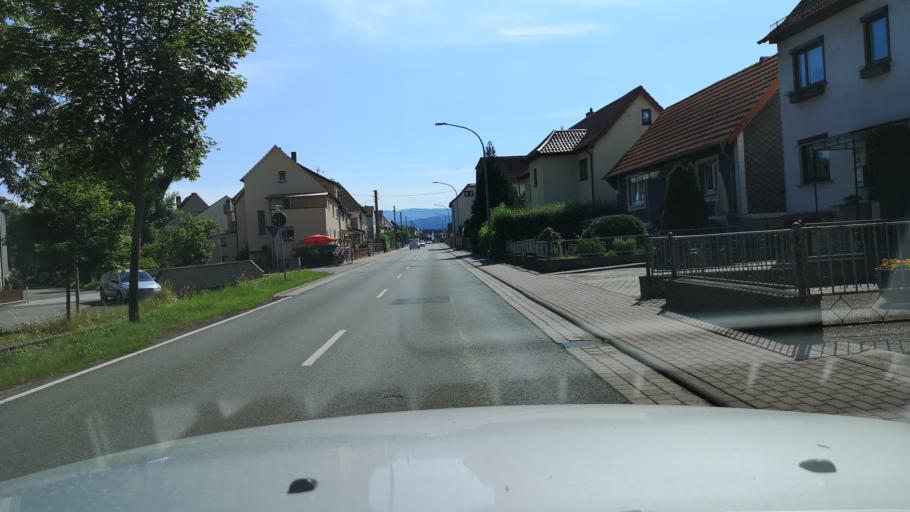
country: DE
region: Thuringia
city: Barchfeld
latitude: 50.8005
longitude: 10.3049
